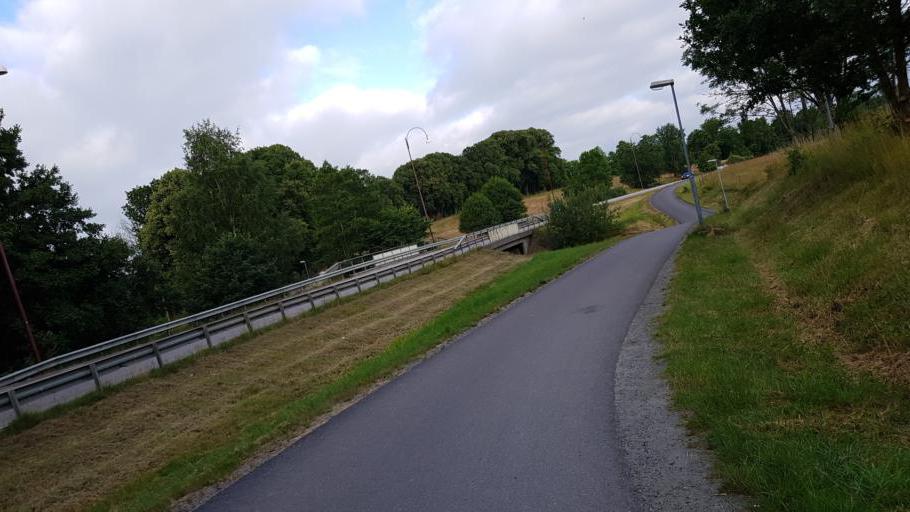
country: SE
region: Vaestra Goetaland
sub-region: Harryda Kommun
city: Molnlycke
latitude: 57.6600
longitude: 12.0966
